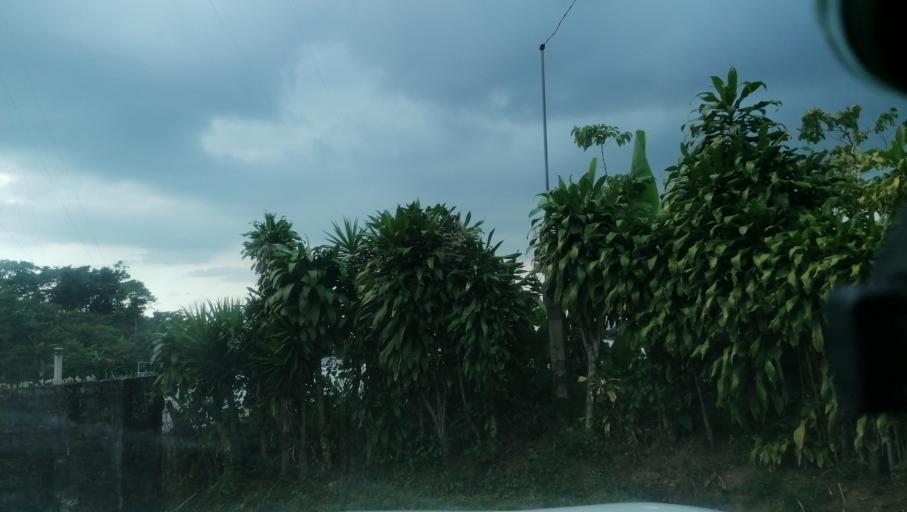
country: MX
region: Chiapas
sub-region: Cacahoatan
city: Benito Juarez
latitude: 15.0707
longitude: -92.1677
